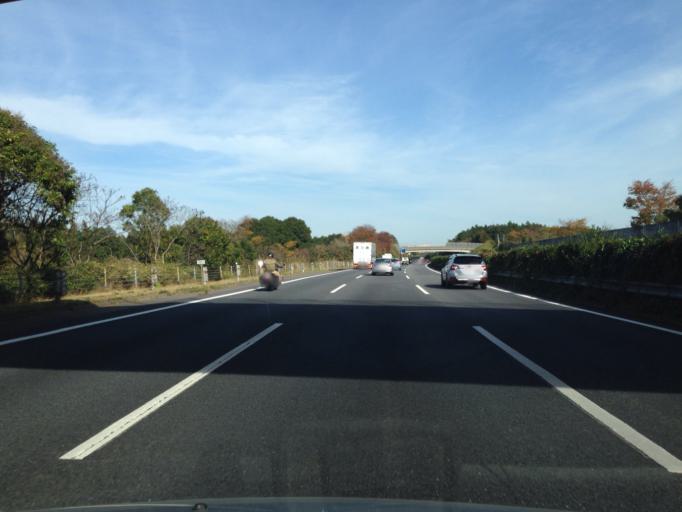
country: JP
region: Ibaraki
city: Ishioka
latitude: 36.2051
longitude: 140.2654
